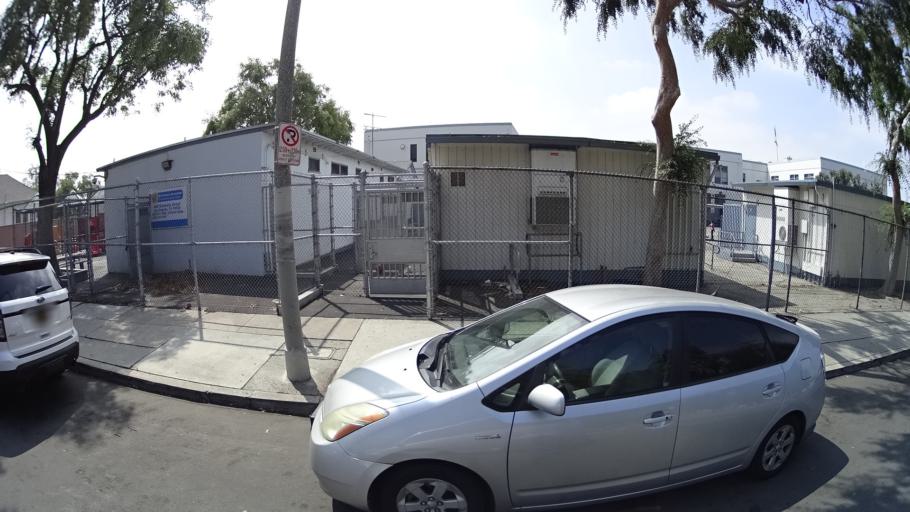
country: US
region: California
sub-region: Los Angeles County
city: Boyle Heights
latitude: 34.0532
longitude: -118.2171
